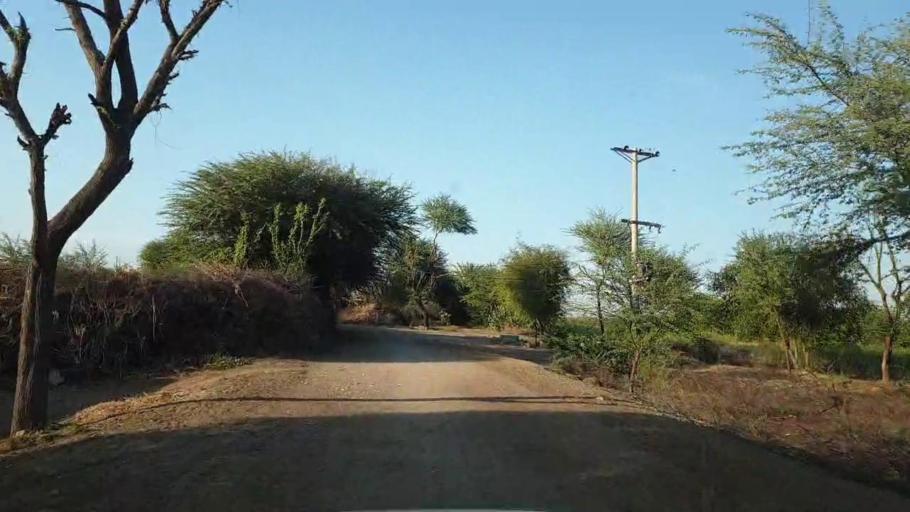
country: PK
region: Sindh
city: Kunri
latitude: 25.0927
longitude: 69.4344
